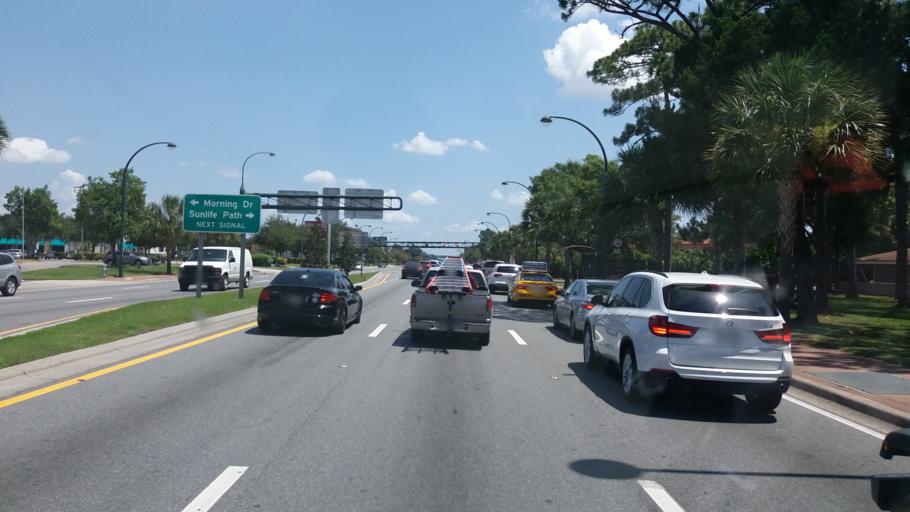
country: US
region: Florida
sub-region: Orange County
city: Sky Lake
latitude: 28.4417
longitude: -81.4032
